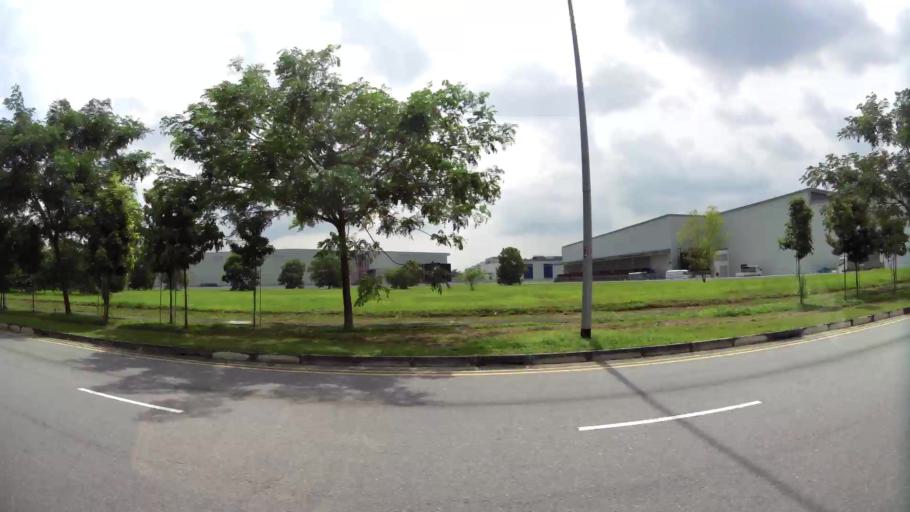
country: MY
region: Johor
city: Kampung Pasir Gudang Baru
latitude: 1.4061
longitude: 103.8564
